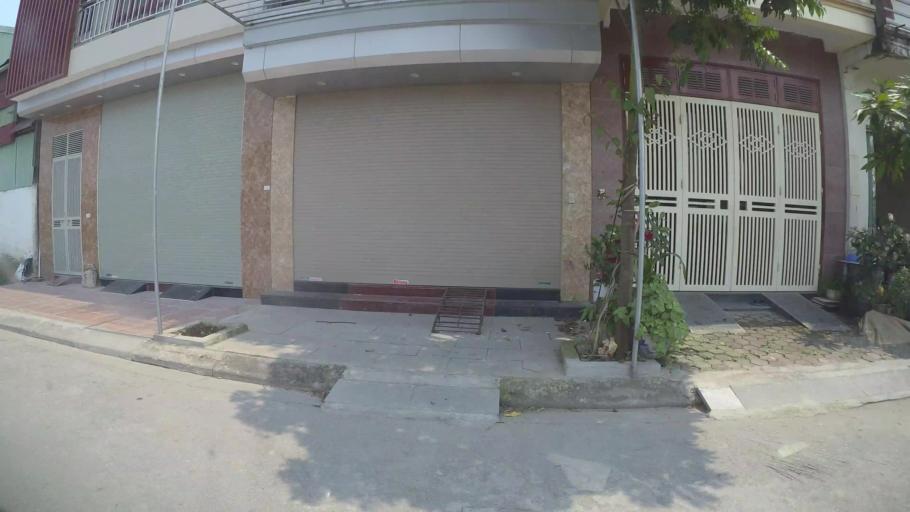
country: VN
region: Ha Noi
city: Ha Dong
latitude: 20.9854
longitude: 105.7726
